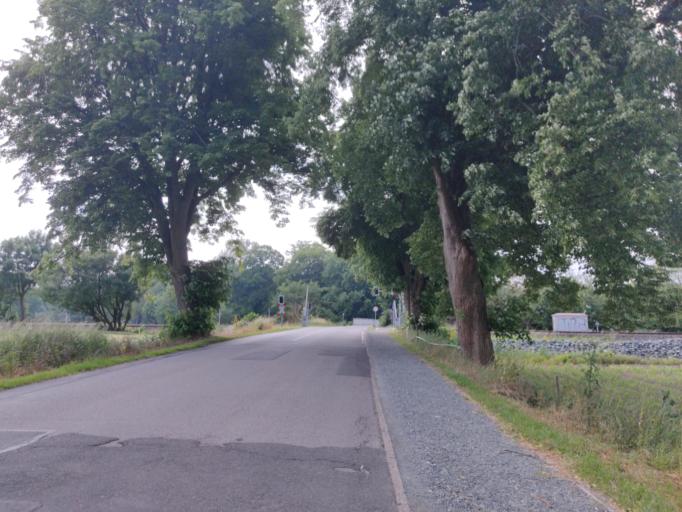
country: DE
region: Lower Saxony
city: Holle
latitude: 52.1003
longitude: 10.1244
